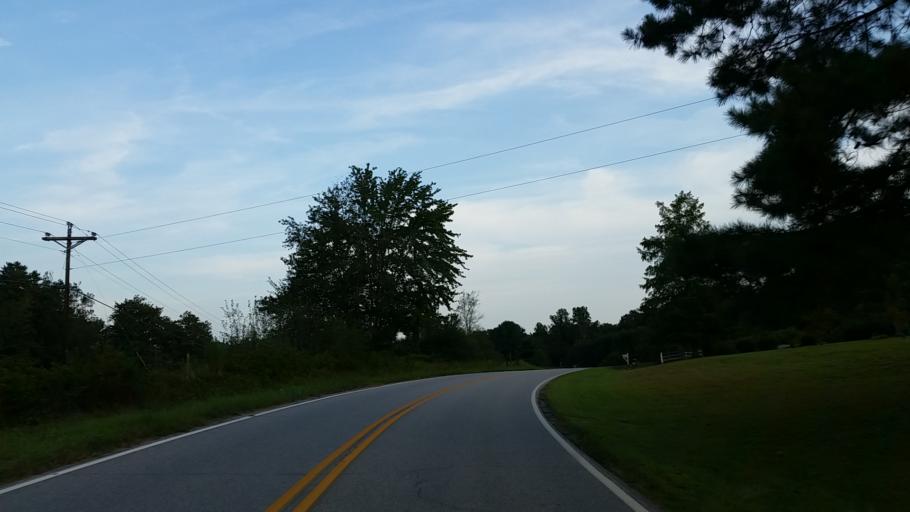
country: US
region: Georgia
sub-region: Lumpkin County
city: Dahlonega
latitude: 34.5803
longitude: -84.0218
